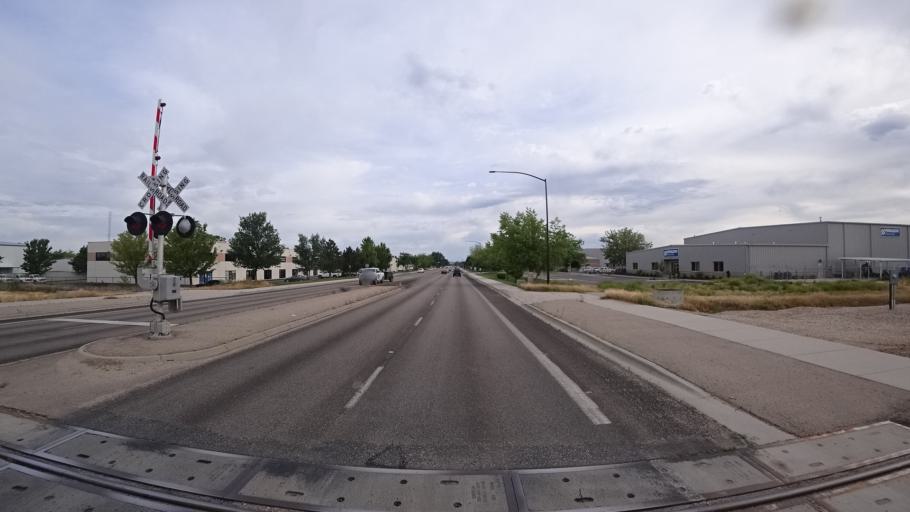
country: US
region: Idaho
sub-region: Ada County
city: Meridian
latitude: 43.6085
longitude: -116.3745
